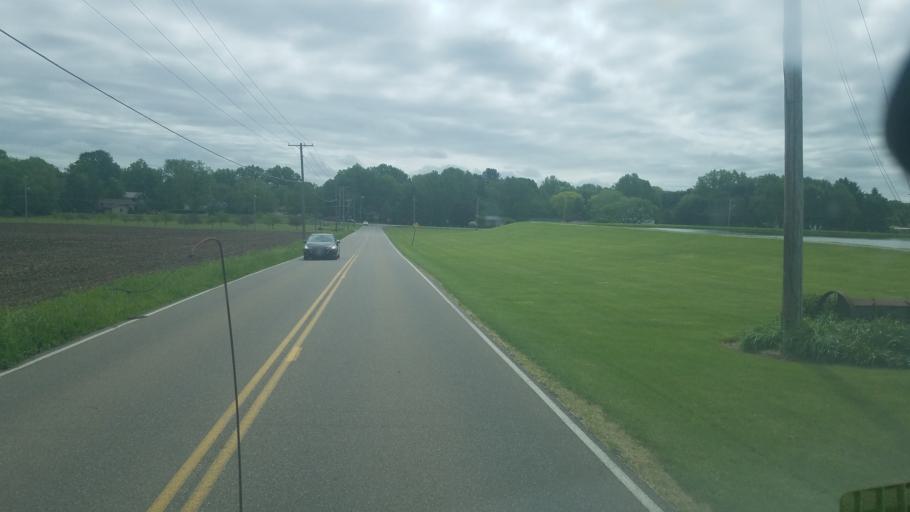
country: US
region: Ohio
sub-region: Wayne County
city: Smithville
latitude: 40.8579
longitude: -81.8706
